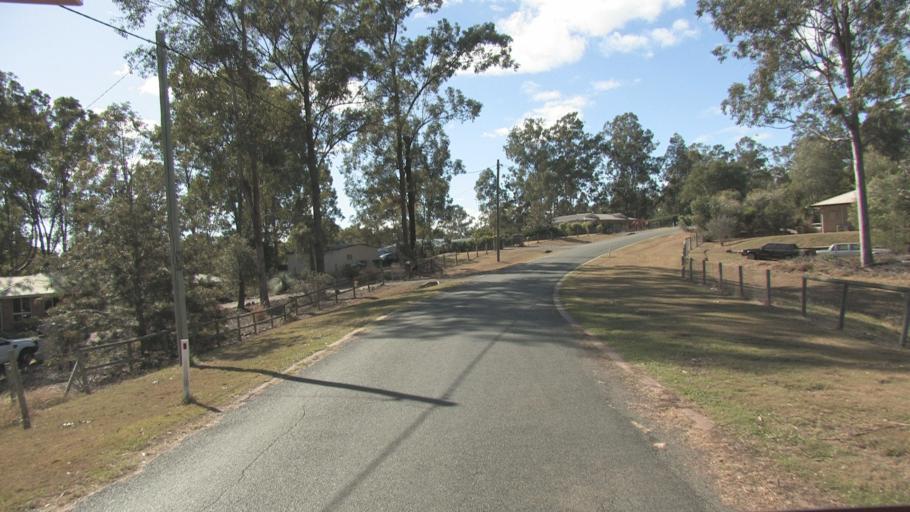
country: AU
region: Queensland
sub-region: Logan
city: Cedar Vale
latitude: -27.8852
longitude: 153.0056
